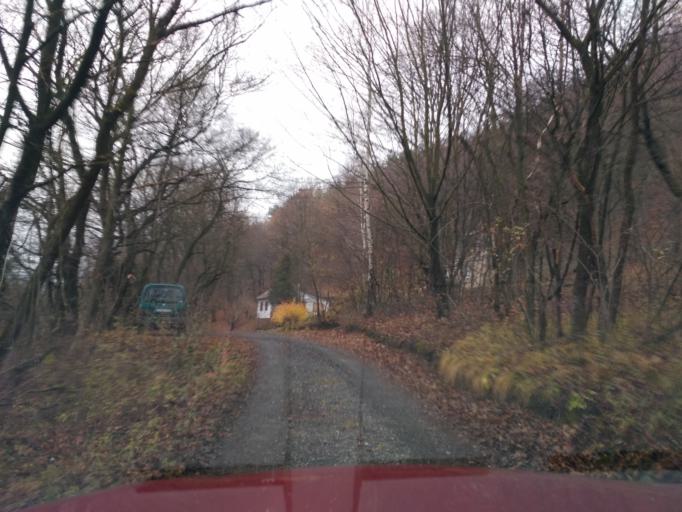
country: SK
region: Kosicky
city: Kosice
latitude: 48.8494
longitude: 21.2311
